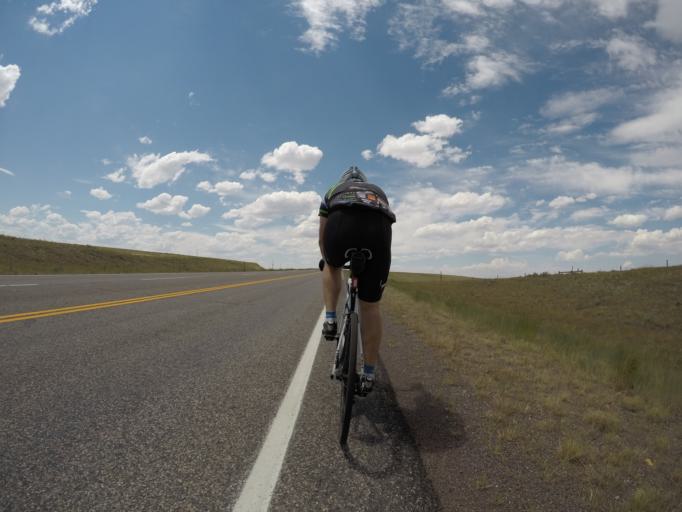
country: US
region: Wyoming
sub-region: Albany County
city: Laramie
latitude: 41.7240
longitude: -105.9328
